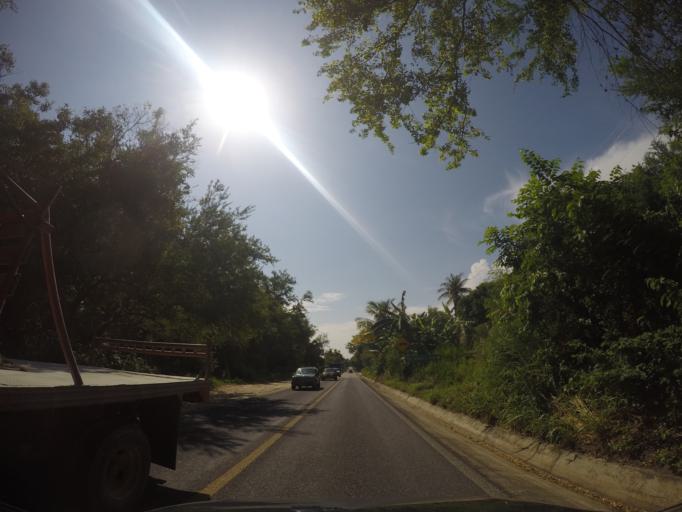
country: MX
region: Oaxaca
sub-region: San Pedro Mixtepec -Dto. 22 -
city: Puerto Escondido
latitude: 15.8849
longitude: -97.1102
